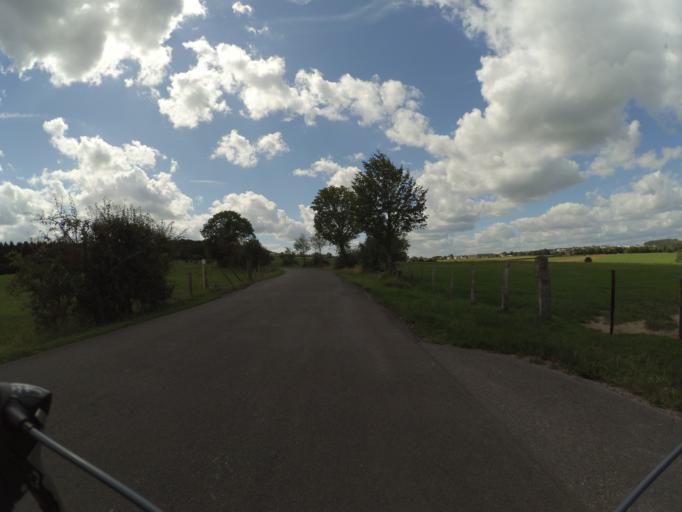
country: DE
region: North Rhine-Westphalia
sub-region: Regierungsbezirk Koln
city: Eschweiler
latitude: 50.7645
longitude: 6.2990
